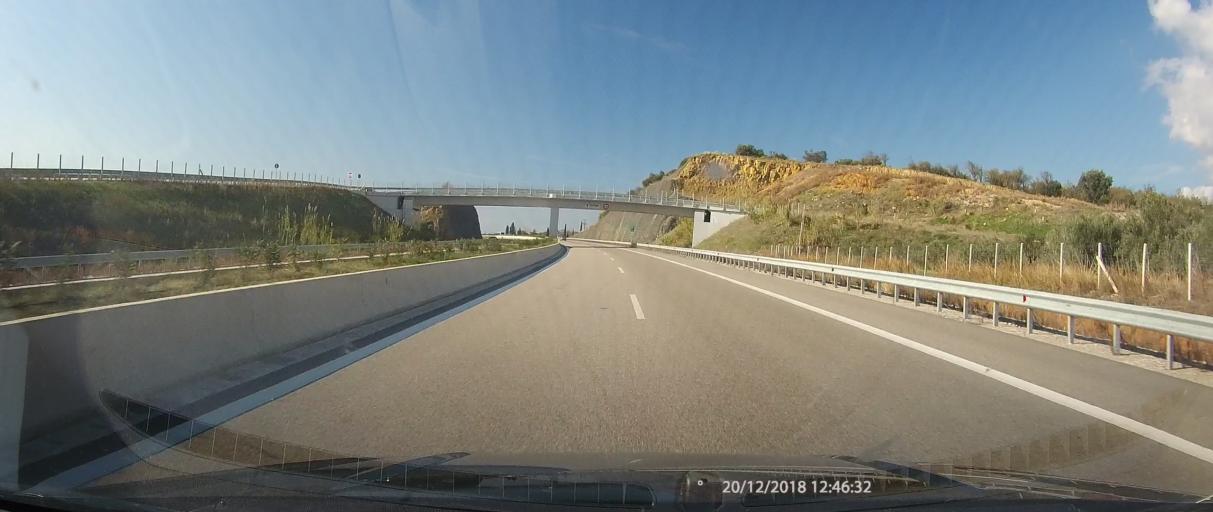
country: GR
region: West Greece
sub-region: Nomos Aitolias kai Akarnanias
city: Mesolongi
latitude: 38.3929
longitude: 21.4713
